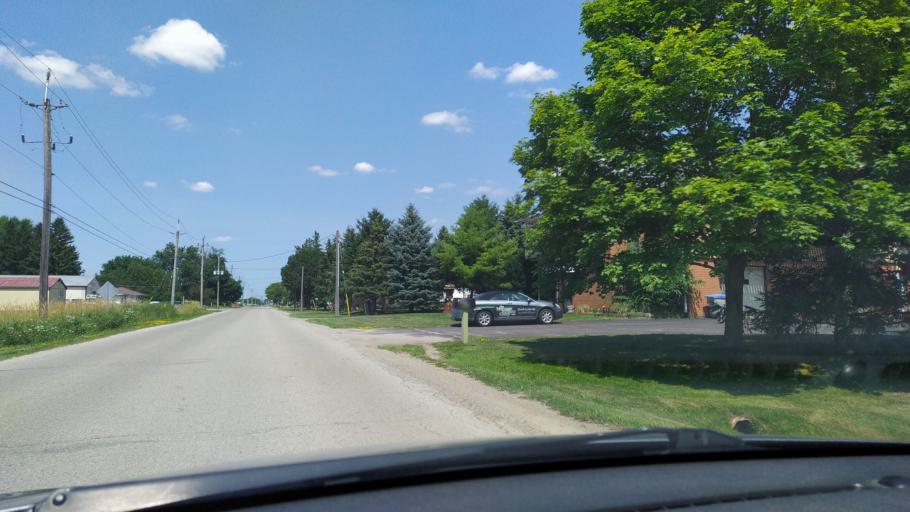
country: CA
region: Ontario
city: Stratford
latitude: 43.3678
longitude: -80.9379
